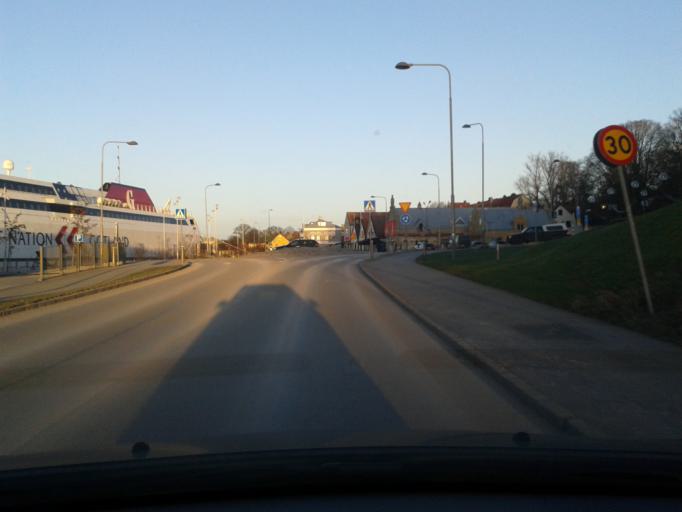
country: SE
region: Gotland
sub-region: Gotland
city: Visby
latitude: 57.6362
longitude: 18.2853
